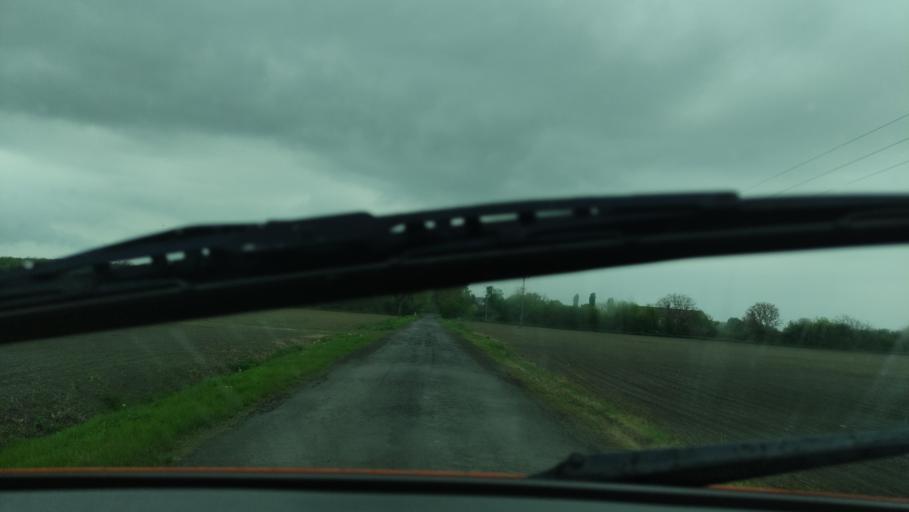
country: HR
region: Osjecko-Baranjska
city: Batina
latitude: 45.9049
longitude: 18.7669
